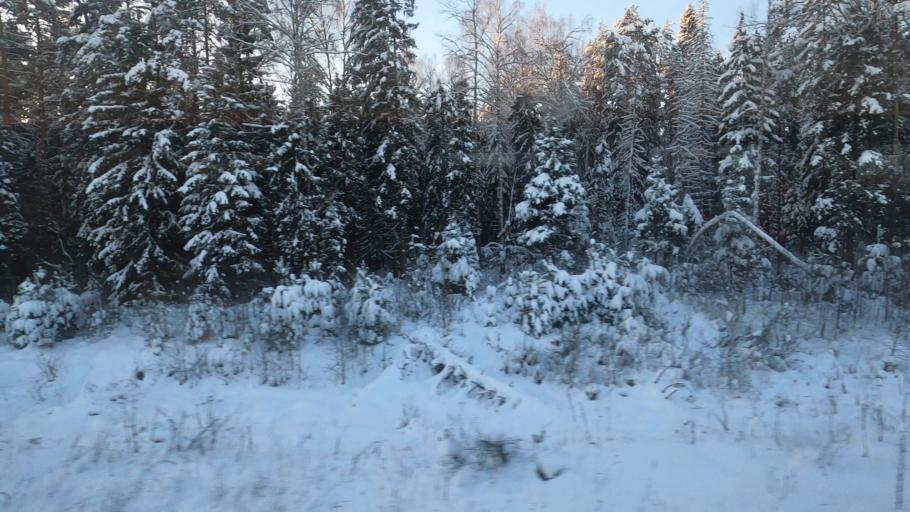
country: RU
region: Moskovskaya
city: Verbilki
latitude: 56.5233
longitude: 37.5579
